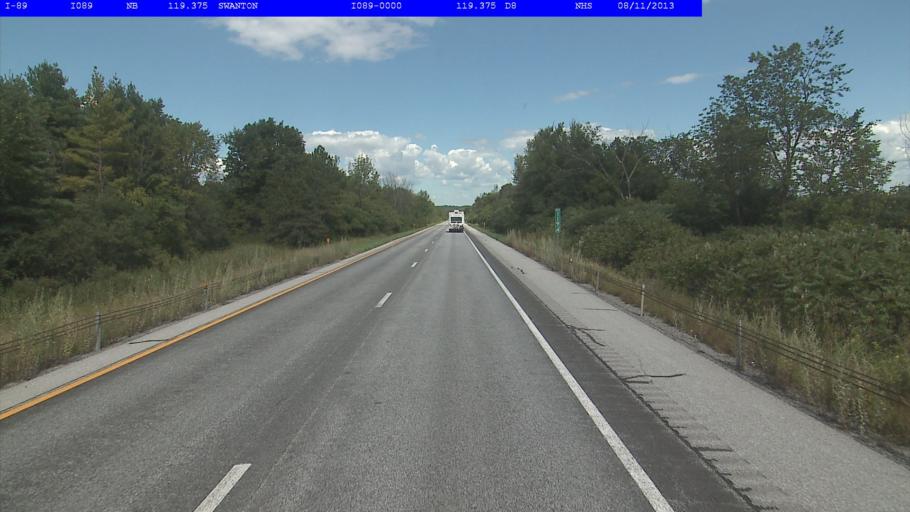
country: US
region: Vermont
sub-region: Franklin County
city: Saint Albans
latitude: 44.8682
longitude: -73.0815
